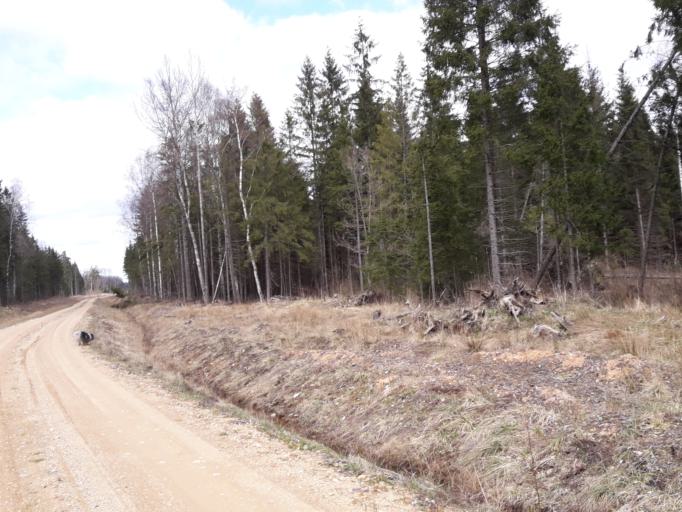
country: LV
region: Broceni
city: Broceni
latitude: 56.8910
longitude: 22.3813
